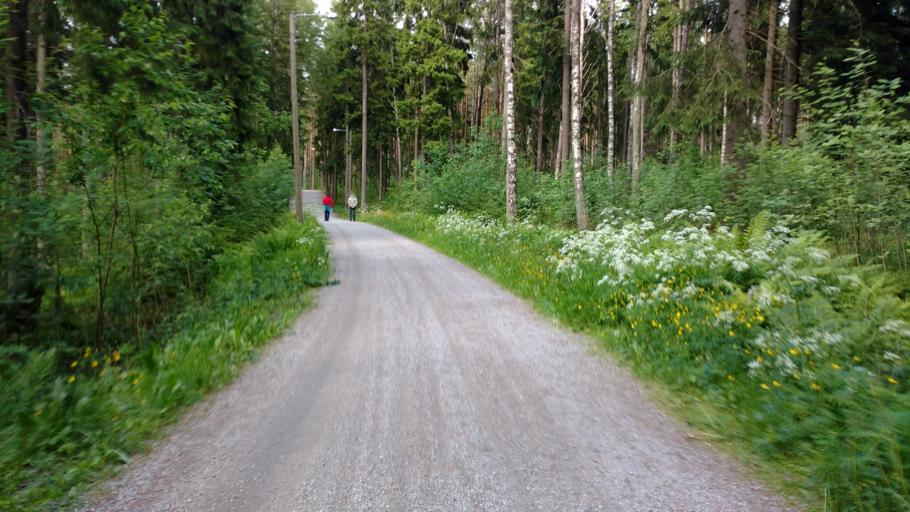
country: FI
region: Varsinais-Suomi
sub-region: Salo
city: Salo
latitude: 60.3880
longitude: 23.1733
